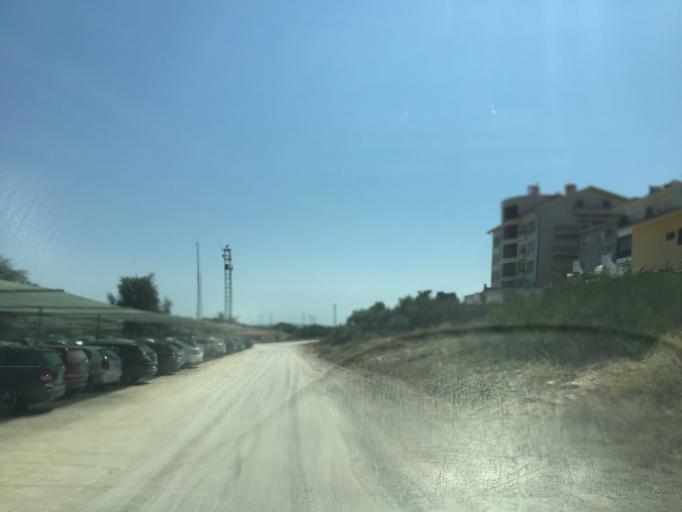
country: PT
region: Coimbra
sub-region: Mira
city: Mira
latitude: 40.3266
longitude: -8.8434
